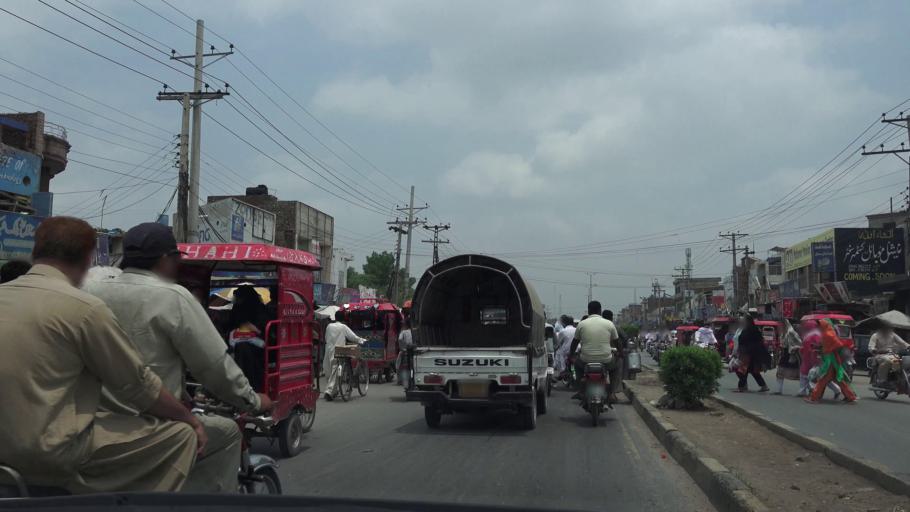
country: PK
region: Punjab
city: Faisalabad
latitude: 31.4038
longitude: 73.1331
